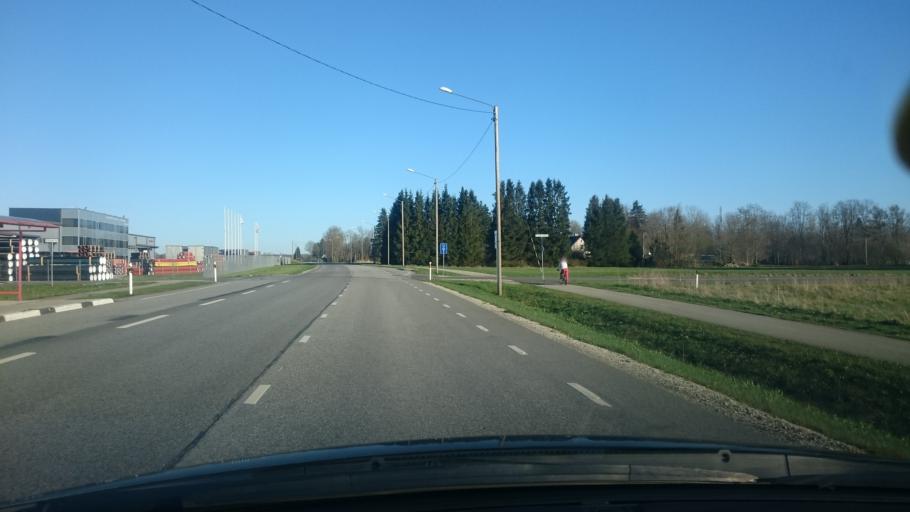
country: EE
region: Harju
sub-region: Kiili vald
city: Kiili
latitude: 59.3386
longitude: 24.8124
